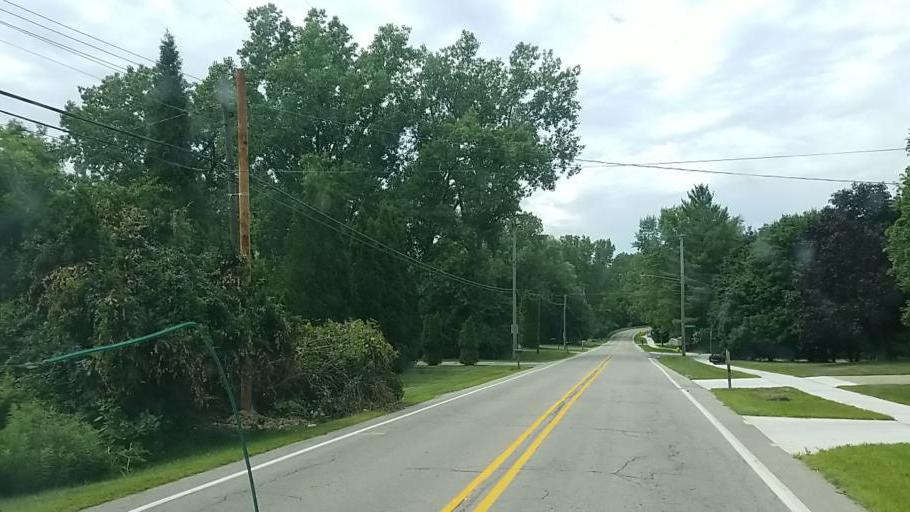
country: US
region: Michigan
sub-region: Kent County
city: Walker
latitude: 42.9980
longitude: -85.7336
